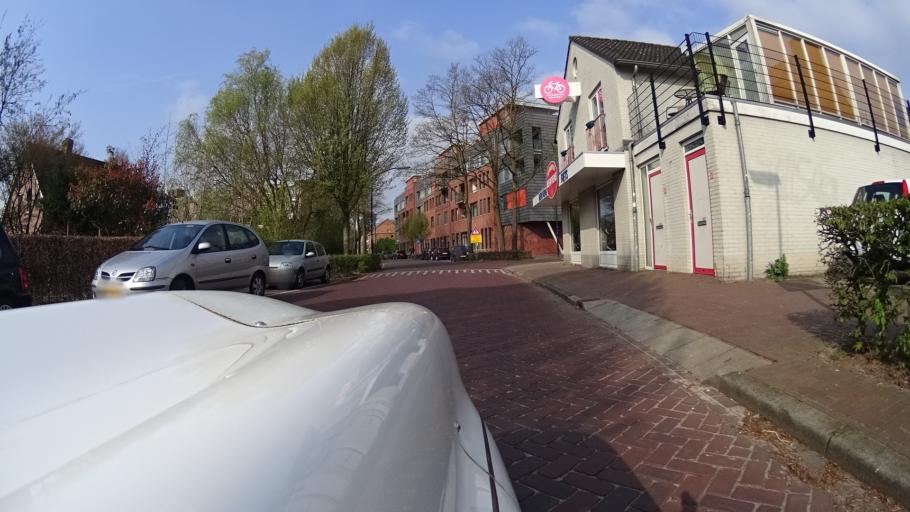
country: NL
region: North Brabant
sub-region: Gemeente Boekel
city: Boekel
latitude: 51.5539
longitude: 5.6861
